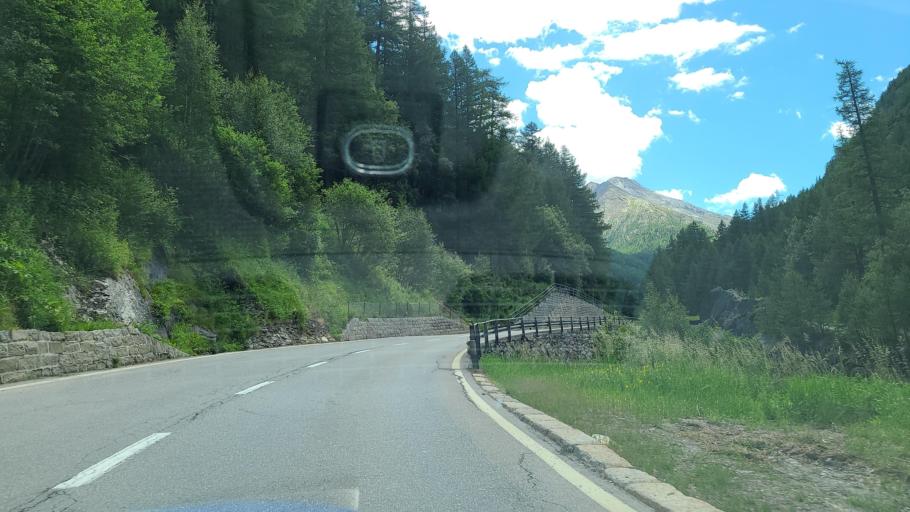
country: CH
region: Valais
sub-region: Visp District
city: Saas-Fee
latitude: 46.1023
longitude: 7.9505
